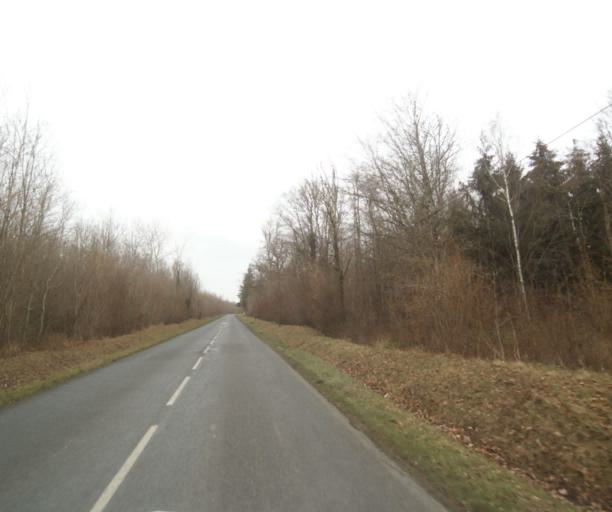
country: FR
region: Champagne-Ardenne
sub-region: Departement de la Haute-Marne
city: Villiers-en-Lieu
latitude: 48.6898
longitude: 4.8890
